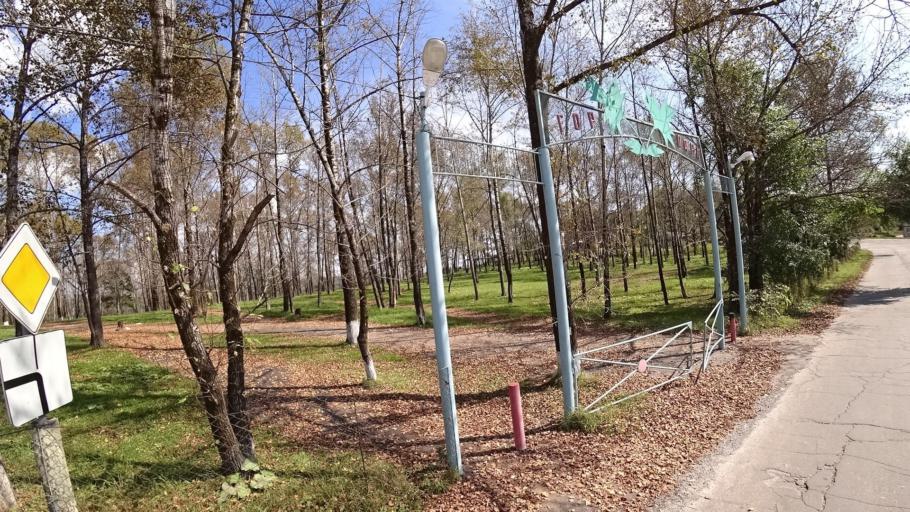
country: RU
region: Jewish Autonomous Oblast
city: Londoko
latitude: 49.0159
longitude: 131.8875
